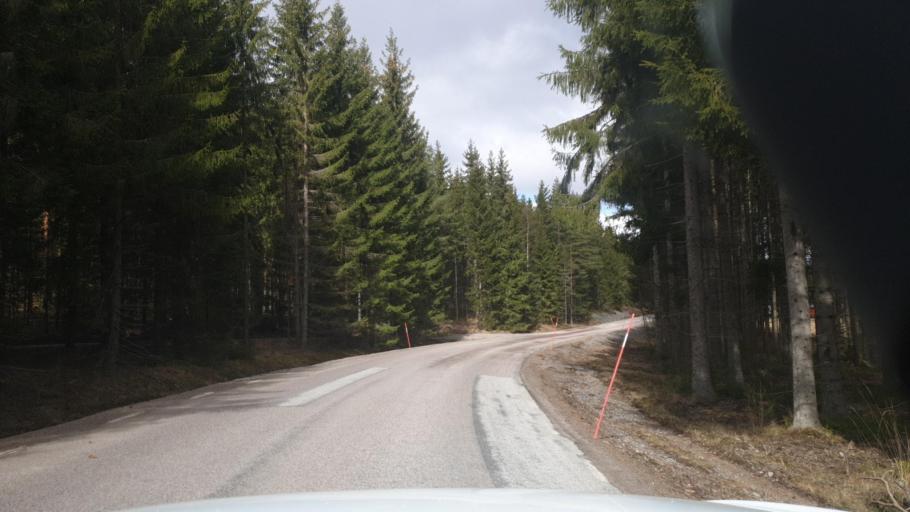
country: SE
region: Vaermland
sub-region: Grums Kommun
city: Grums
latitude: 59.5026
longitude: 12.8719
